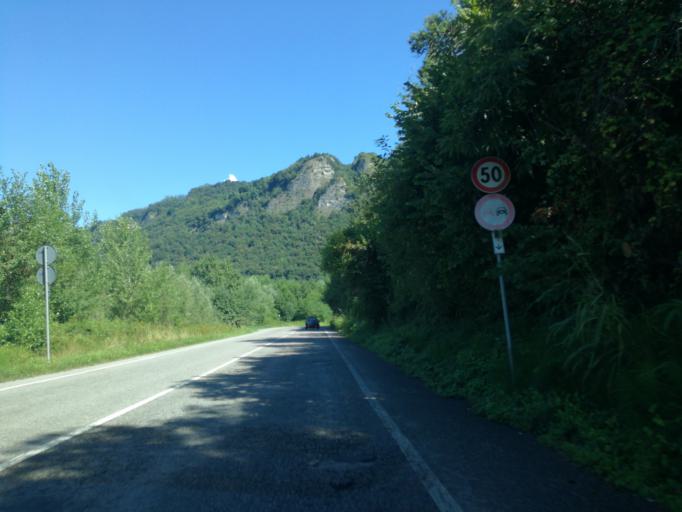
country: IT
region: Lombardy
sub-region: Provincia di Bergamo
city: Cisano Bergamasco
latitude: 45.7460
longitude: 9.4605
